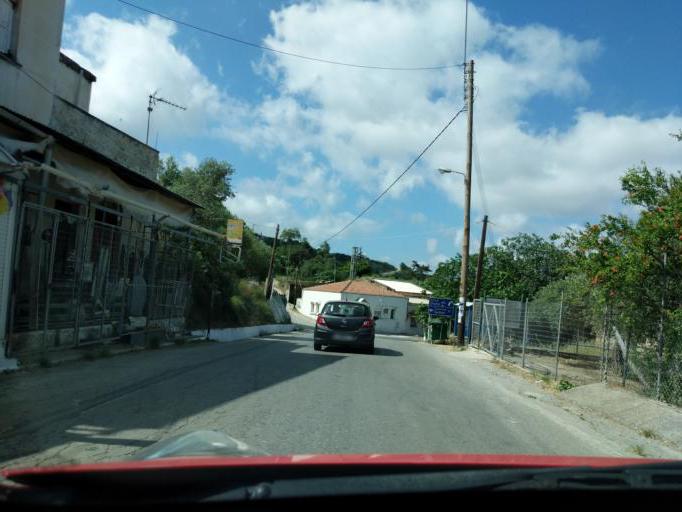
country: GR
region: Crete
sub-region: Nomos Chanias
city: Kissamos
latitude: 35.4303
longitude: 23.6852
